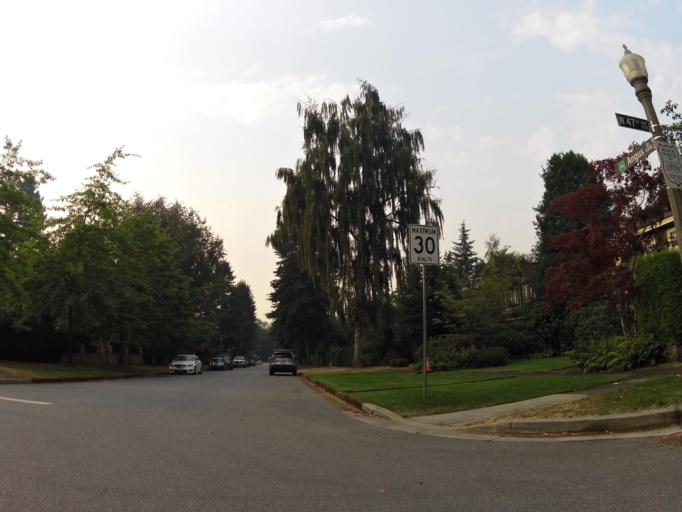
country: CA
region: British Columbia
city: Vancouver
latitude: 49.2289
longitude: -123.1480
